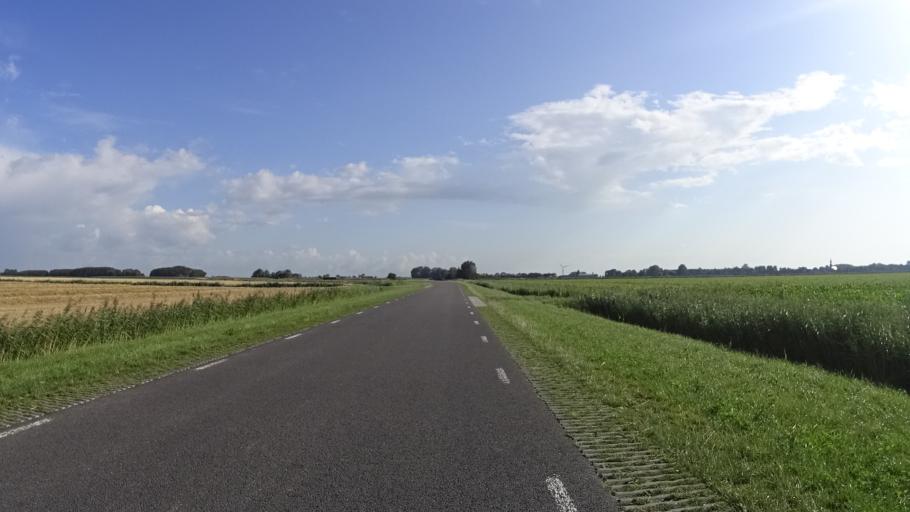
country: NL
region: Friesland
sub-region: Gemeente Harlingen
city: Harlingen
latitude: 53.1259
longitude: 5.4567
